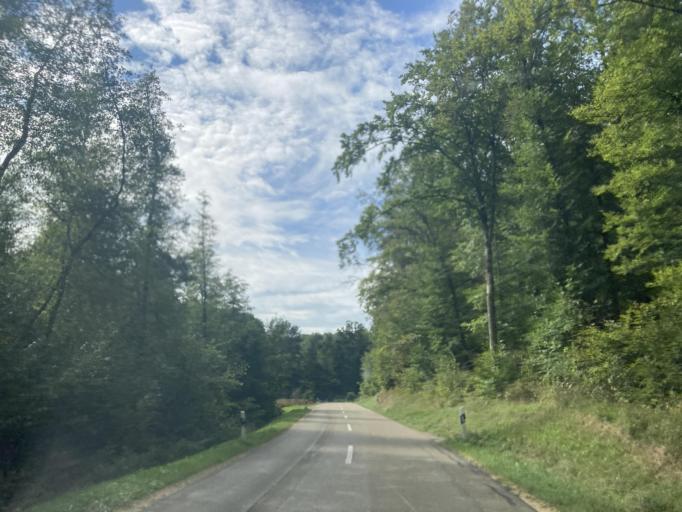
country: DE
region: Bavaria
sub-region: Swabia
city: Forheim
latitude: 48.7704
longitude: 10.4617
